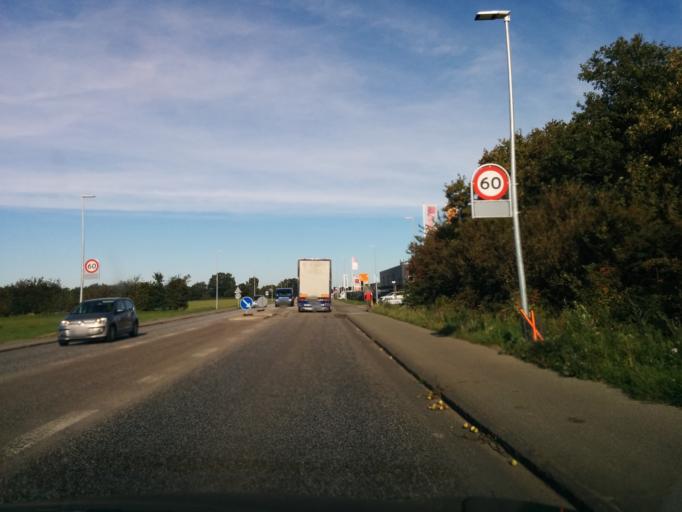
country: DK
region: South Denmark
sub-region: Kolding Kommune
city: Kolding
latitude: 55.4610
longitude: 9.4734
